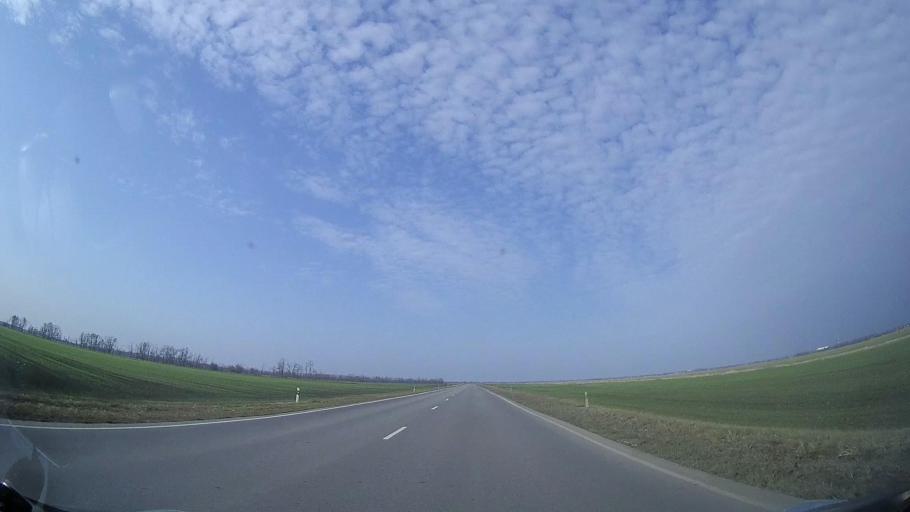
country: RU
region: Rostov
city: Tselina
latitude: 46.5129
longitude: 41.0558
